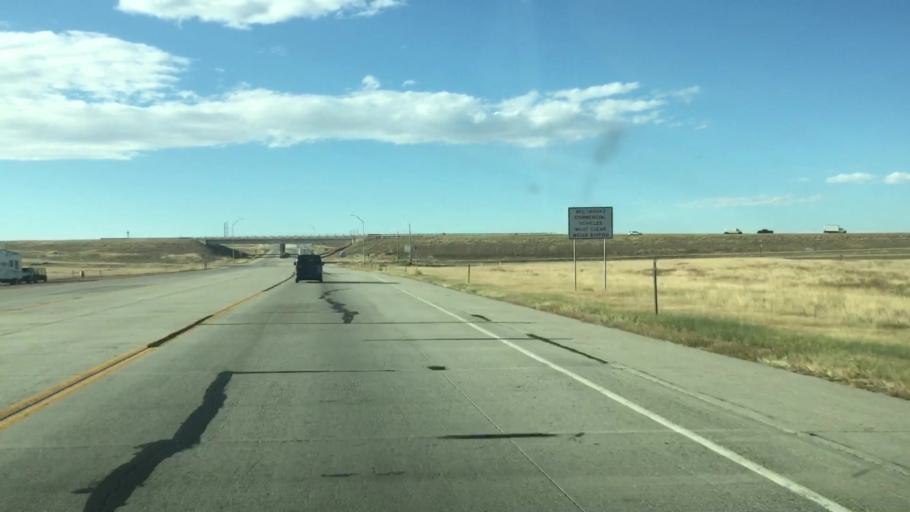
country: US
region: Colorado
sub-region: Lincoln County
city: Limon
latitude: 39.2601
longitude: -103.6439
